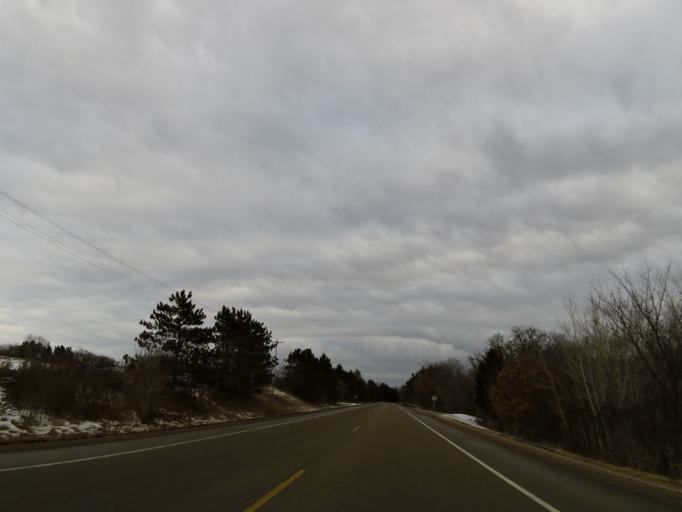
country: US
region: Wisconsin
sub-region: Saint Croix County
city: North Hudson
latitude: 45.0227
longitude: -92.7458
